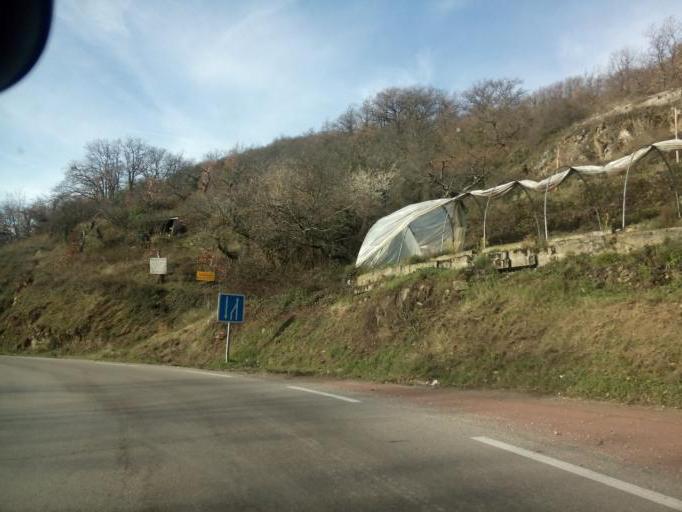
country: FR
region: Rhone-Alpes
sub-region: Departement de l'Ardeche
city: Serrieres
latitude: 45.3123
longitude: 4.7678
